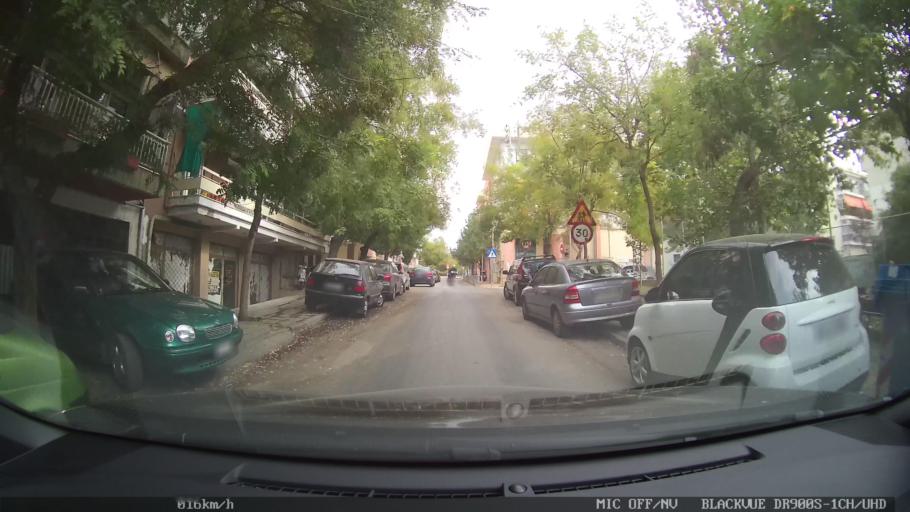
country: GR
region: Central Macedonia
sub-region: Nomos Thessalonikis
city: Triandria
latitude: 40.6100
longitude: 22.9698
